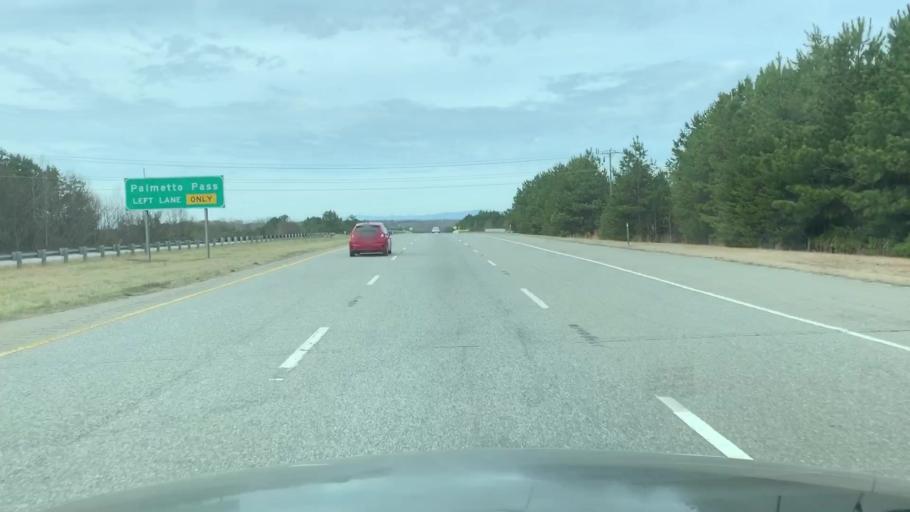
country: US
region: South Carolina
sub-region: Greenville County
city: Golden Grove
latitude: 34.7421
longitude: -82.4363
